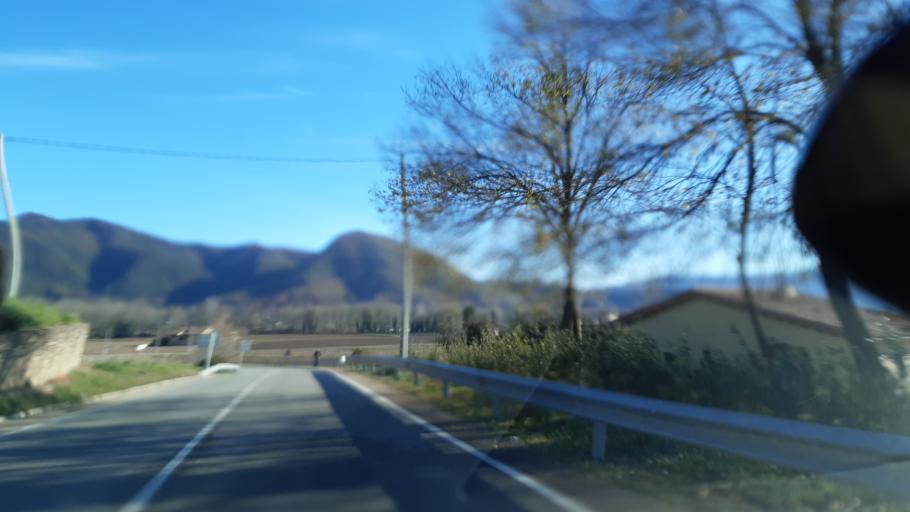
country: ES
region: Catalonia
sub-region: Provincia de Girona
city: Bas
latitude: 42.1474
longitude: 2.4385
